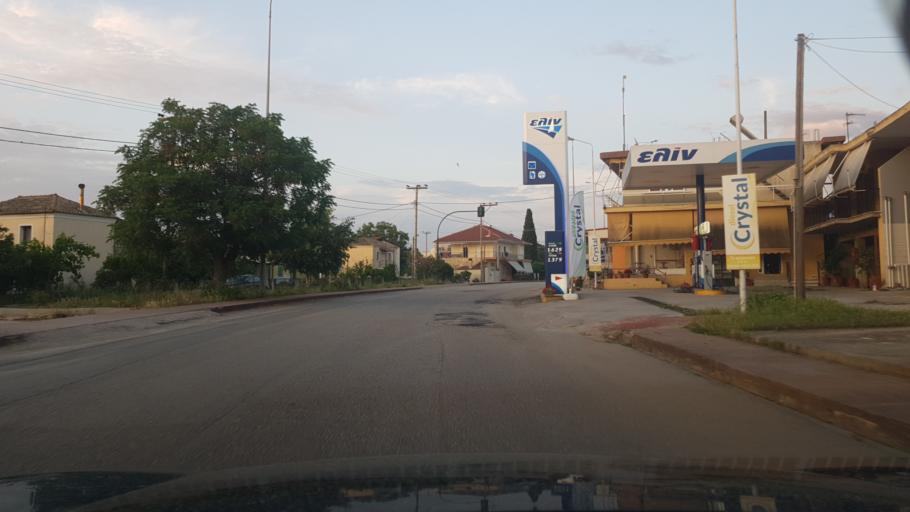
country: GR
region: West Greece
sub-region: Nomos Aitolias kai Akarnanias
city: Vonitsa
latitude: 38.8696
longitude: 20.8048
